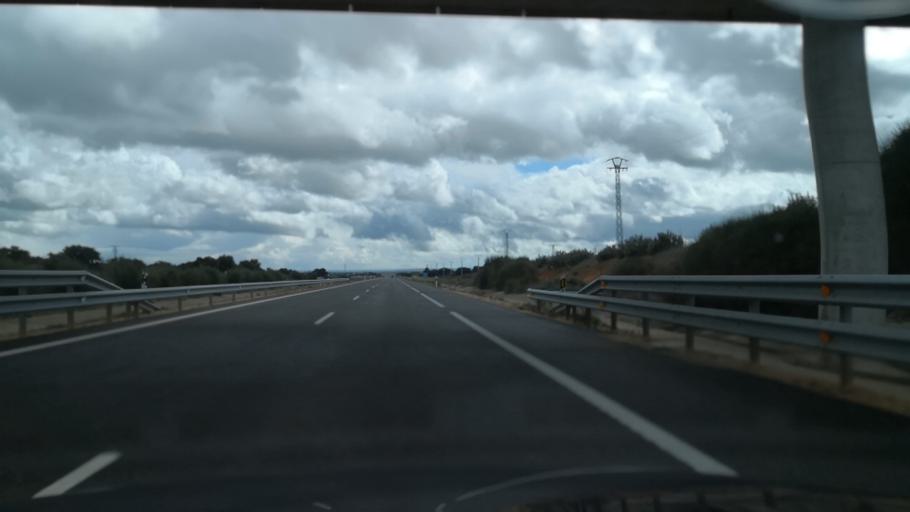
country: ES
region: Castille and Leon
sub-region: Provincia de Salamanca
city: Topas
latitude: 41.1615
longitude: -5.6958
